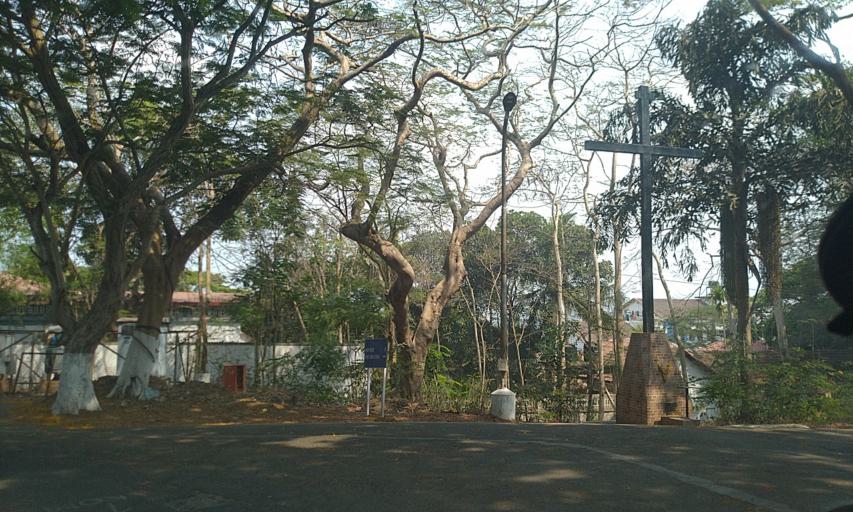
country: IN
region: Goa
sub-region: North Goa
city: Panaji
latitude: 15.4924
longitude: 73.8263
